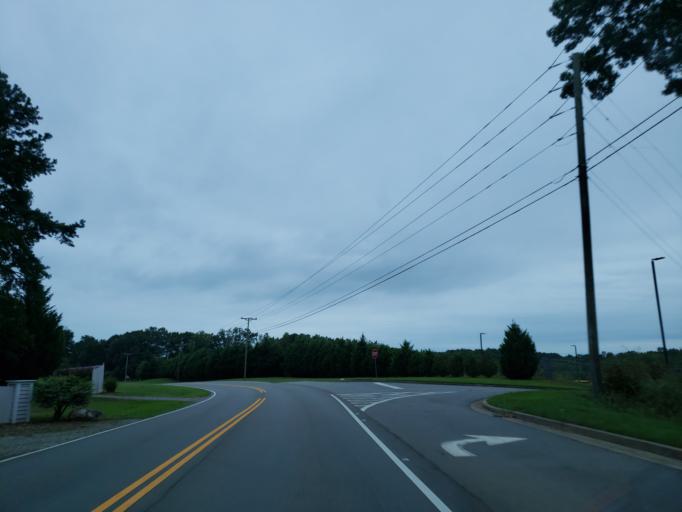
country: US
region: Georgia
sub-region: Cherokee County
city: Canton
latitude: 34.3266
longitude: -84.4688
